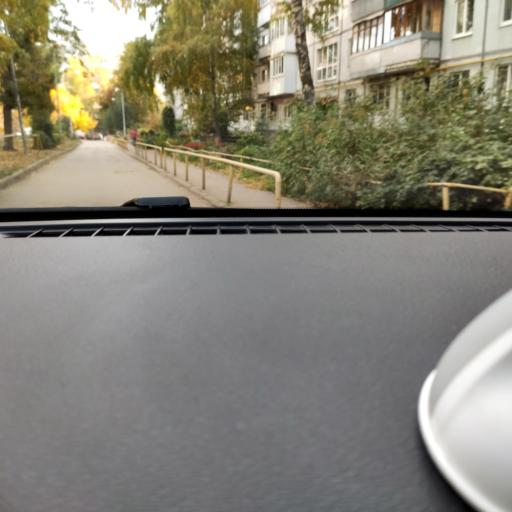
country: RU
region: Samara
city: Samara
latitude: 53.2356
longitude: 50.2153
